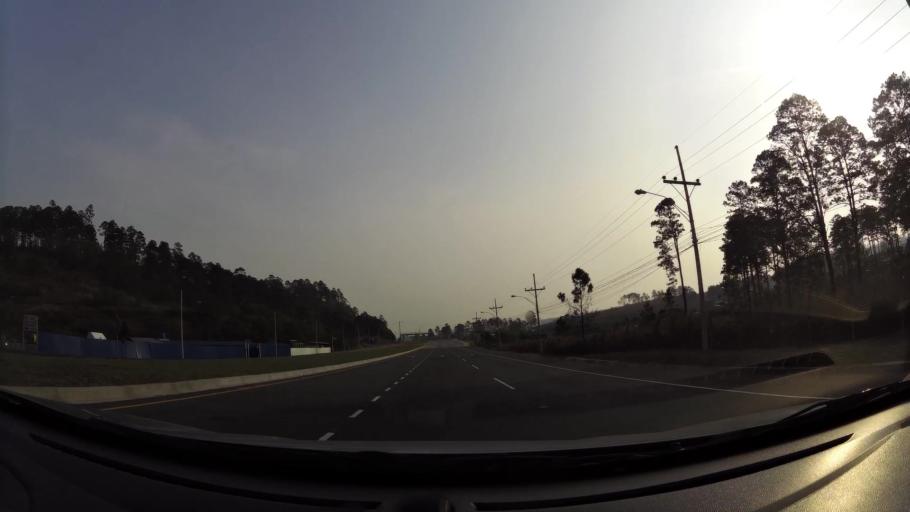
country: HN
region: Francisco Morazan
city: Tamara
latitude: 14.1710
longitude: -87.3136
